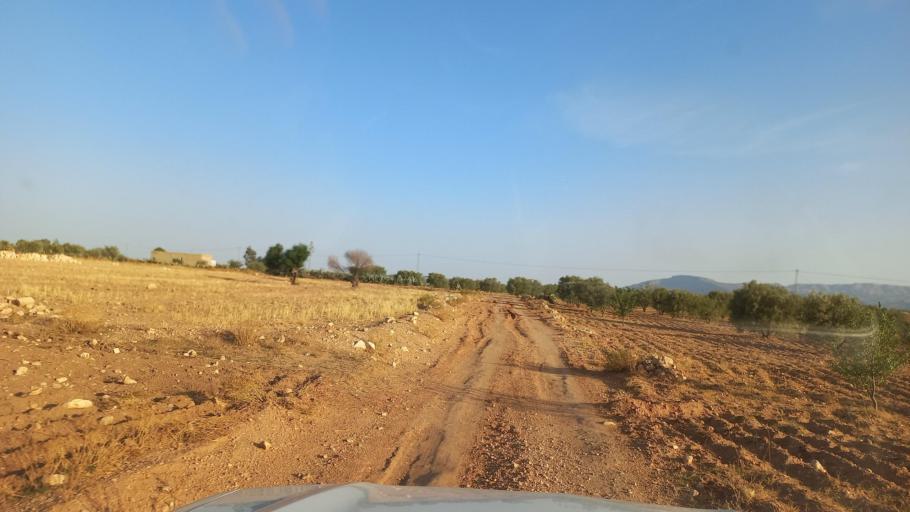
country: TN
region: Al Qasrayn
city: Kasserine
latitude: 35.2574
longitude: 8.9072
